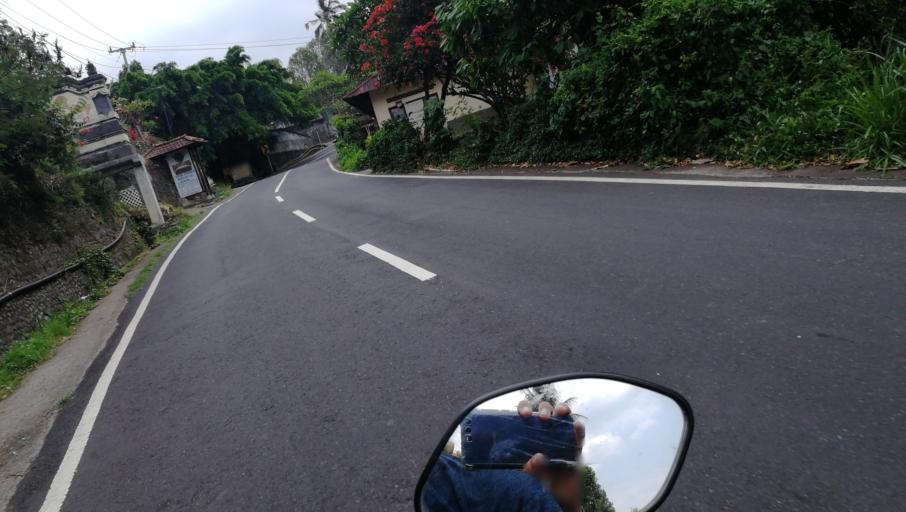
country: ID
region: Bali
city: Munduk
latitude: -8.2634
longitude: 115.0619
